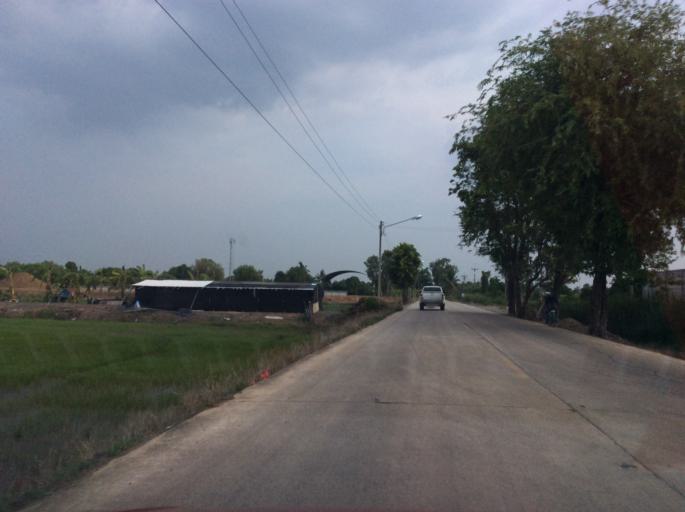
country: TH
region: Pathum Thani
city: Thanyaburi
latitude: 13.9767
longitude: 100.7266
